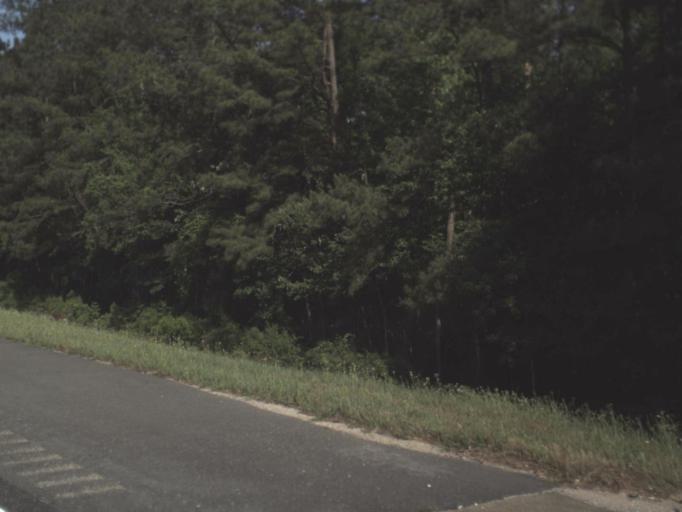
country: US
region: Florida
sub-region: Holmes County
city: Bonifay
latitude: 30.7537
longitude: -85.8444
